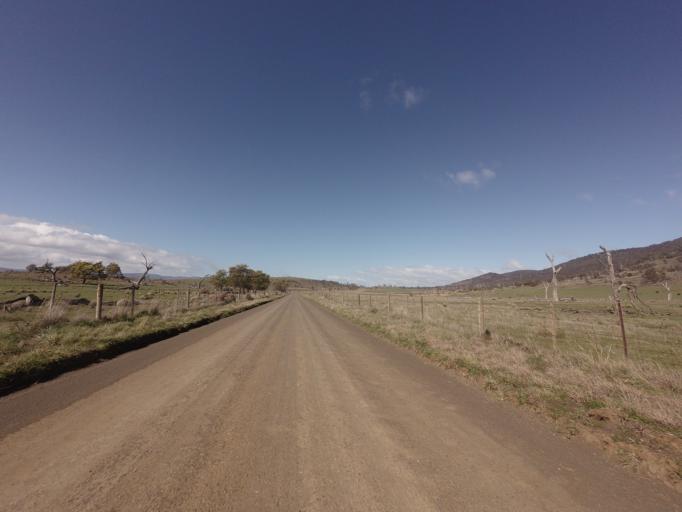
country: AU
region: Tasmania
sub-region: Northern Midlands
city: Evandale
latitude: -41.9268
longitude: 147.4109
